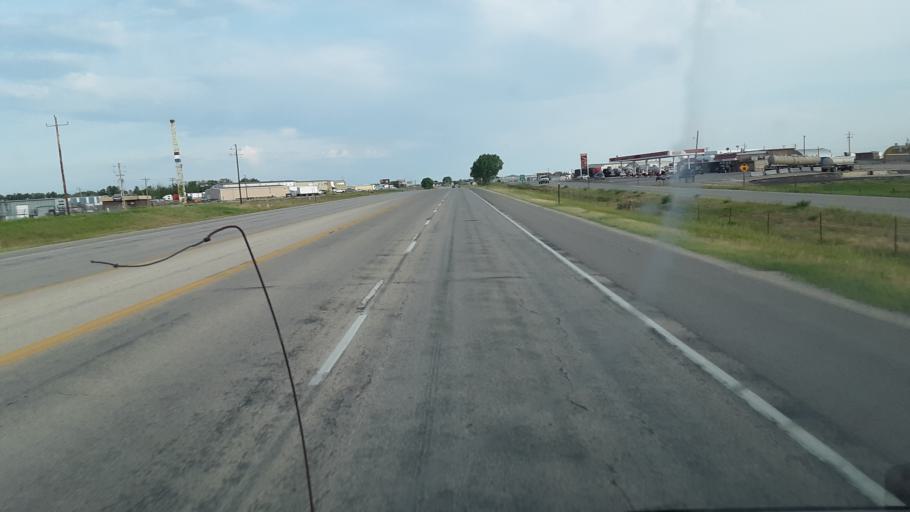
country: US
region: Wyoming
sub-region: Natrona County
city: Mills
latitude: 42.8742
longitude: -106.4235
